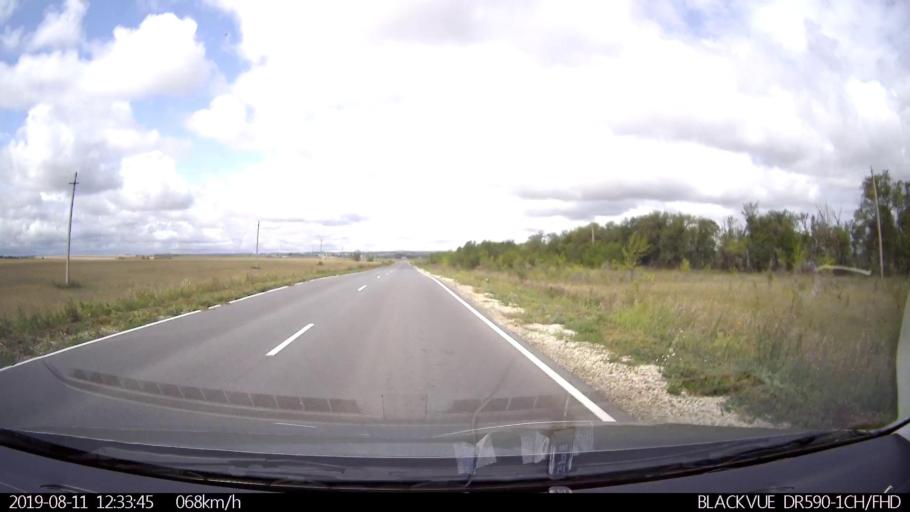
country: RU
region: Ulyanovsk
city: Ignatovka
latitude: 53.8118
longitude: 47.8518
